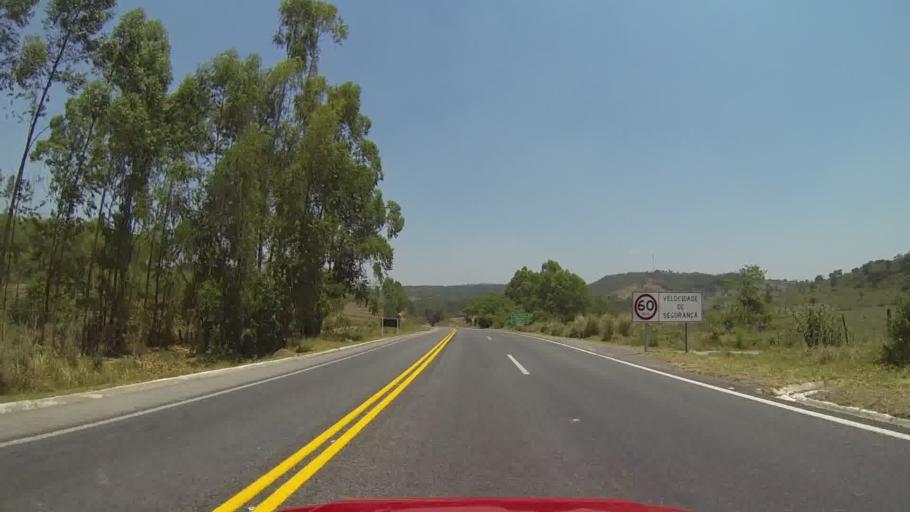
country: BR
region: Minas Gerais
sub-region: Itapecerica
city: Itapecerica
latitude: -20.2944
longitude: -45.1754
